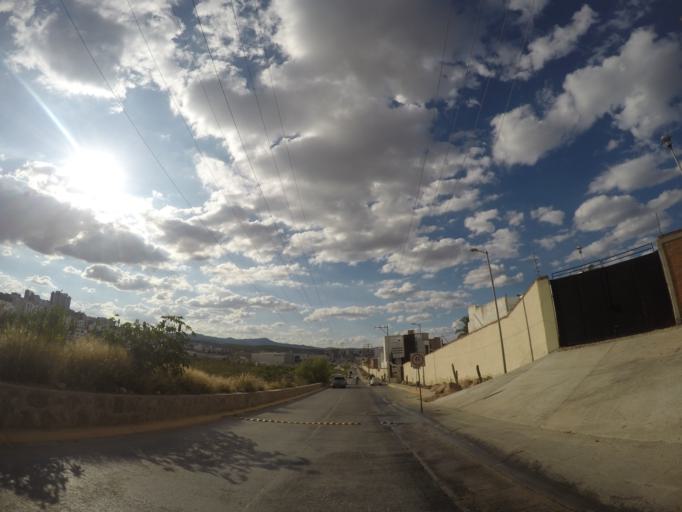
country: MX
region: San Luis Potosi
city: Escalerillas
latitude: 22.1229
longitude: -101.0246
